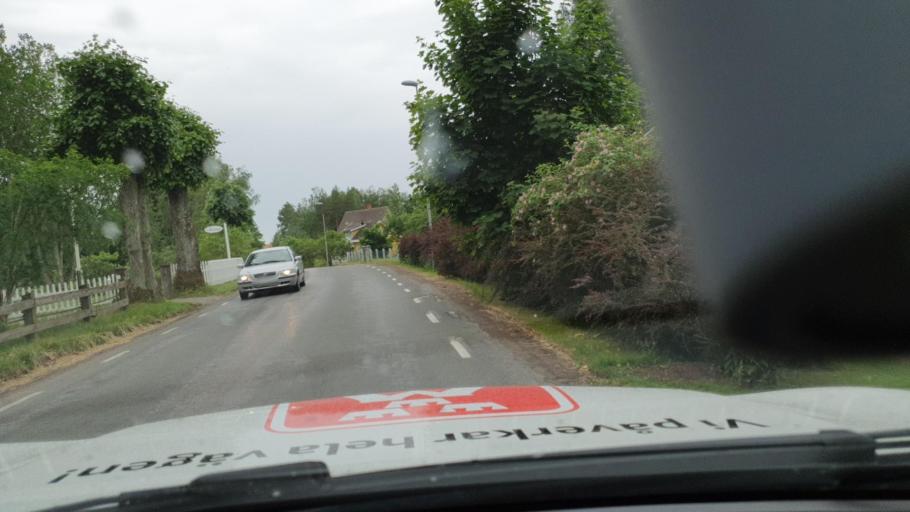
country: SE
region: Vaestra Goetaland
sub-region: Tidaholms Kommun
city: Olofstorp
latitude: 58.3432
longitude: 14.0470
